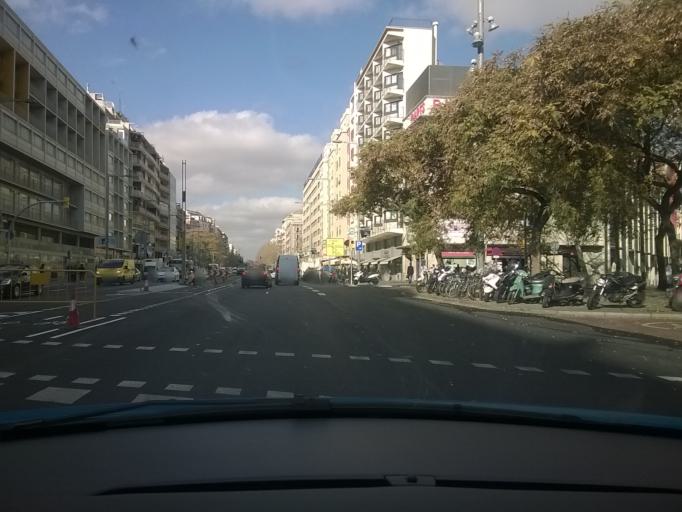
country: ES
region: Catalonia
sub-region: Provincia de Barcelona
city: Ciutat Vella
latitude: 41.3751
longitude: 2.1701
